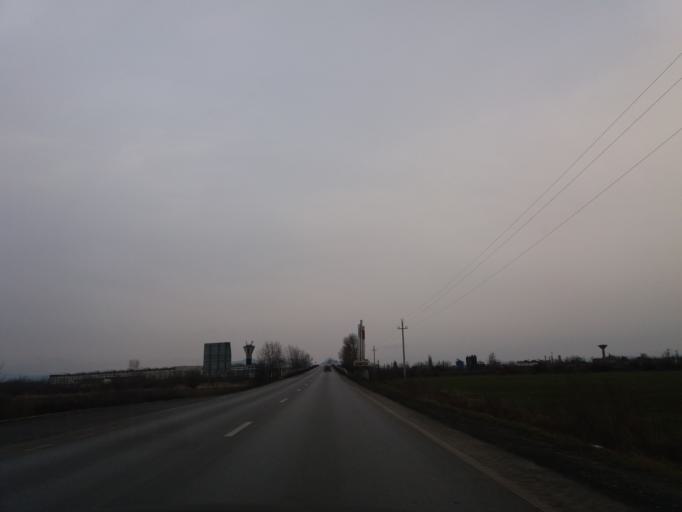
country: RO
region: Hunedoara
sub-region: Oras Simeria
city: Simeria
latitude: 45.8366
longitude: 23.0315
